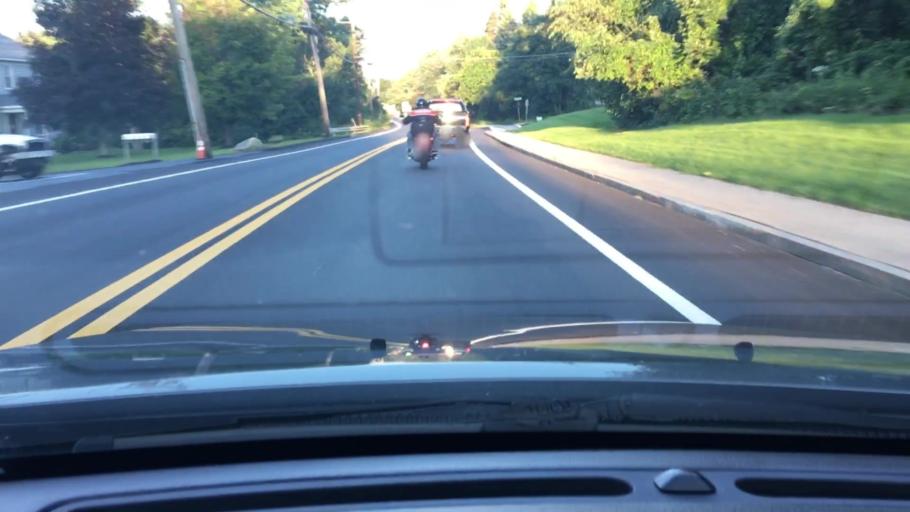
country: US
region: Massachusetts
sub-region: Worcester County
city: Grafton
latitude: 42.2302
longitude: -71.7156
